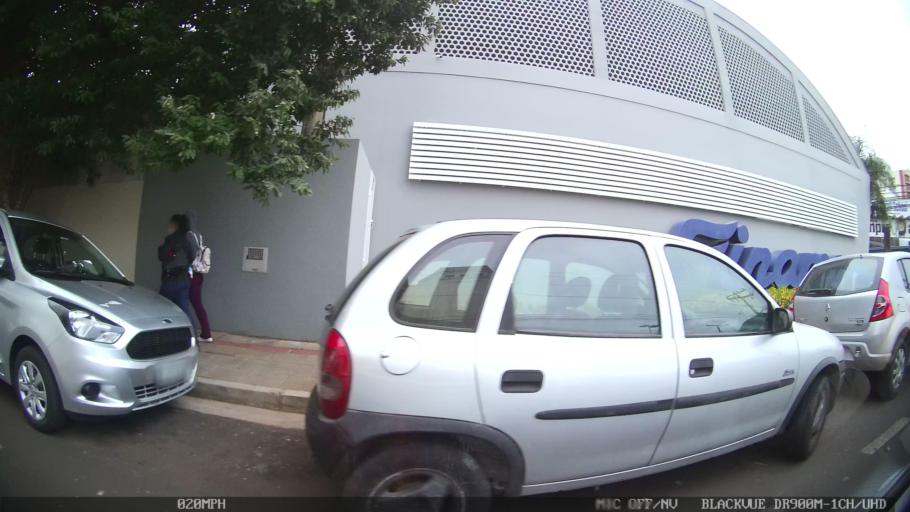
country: BR
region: Sao Paulo
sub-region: Sao Jose Do Rio Preto
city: Sao Jose do Rio Preto
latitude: -20.8205
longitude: -49.3917
